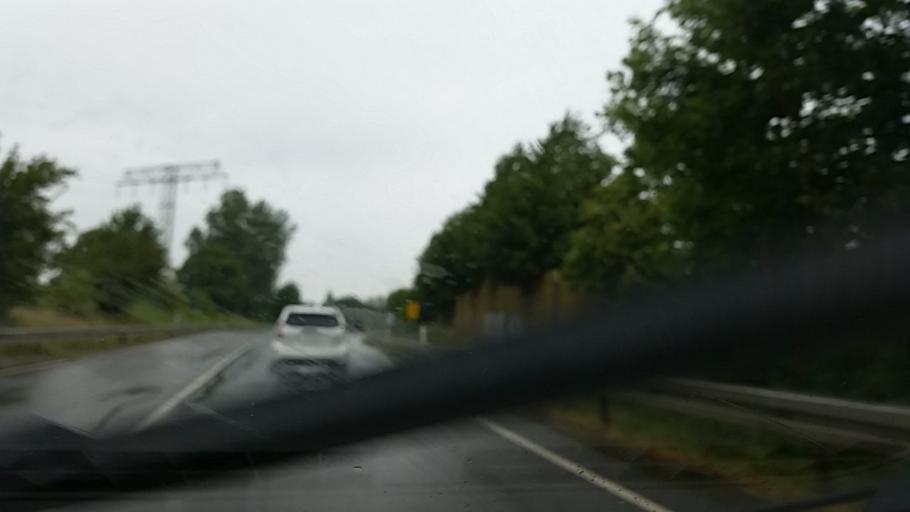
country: DE
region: Mecklenburg-Vorpommern
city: Kropelin
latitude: 54.0746
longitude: 11.7865
